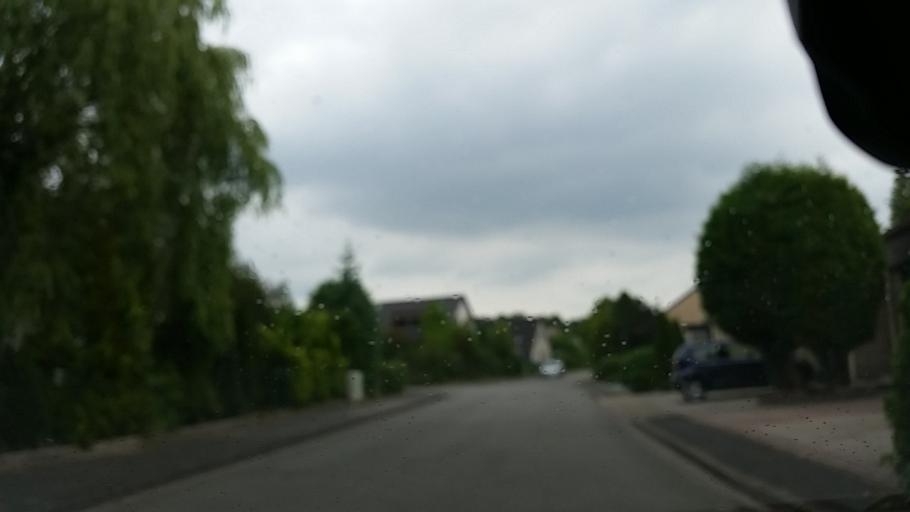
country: DE
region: Lower Saxony
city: Wolfsburg
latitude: 52.4548
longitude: 10.7892
